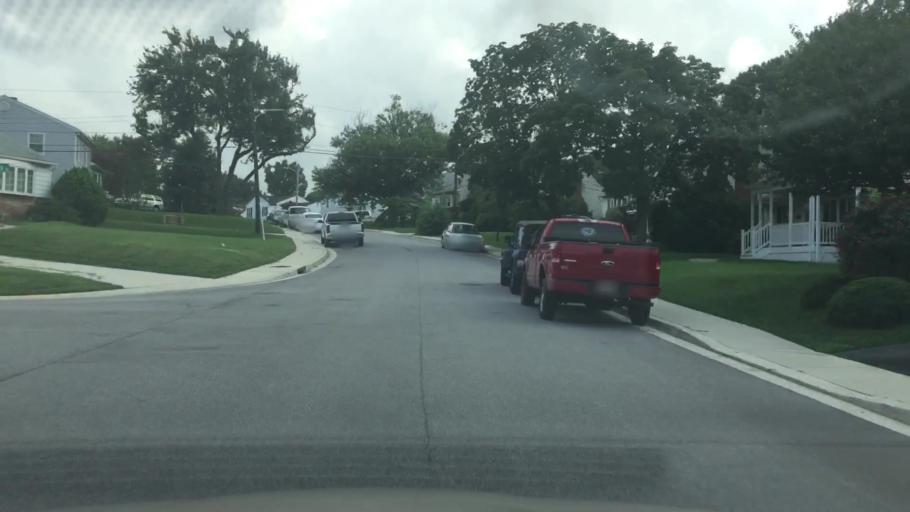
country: US
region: Maryland
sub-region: Anne Arundel County
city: South Gate
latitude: 39.1431
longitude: -76.6430
